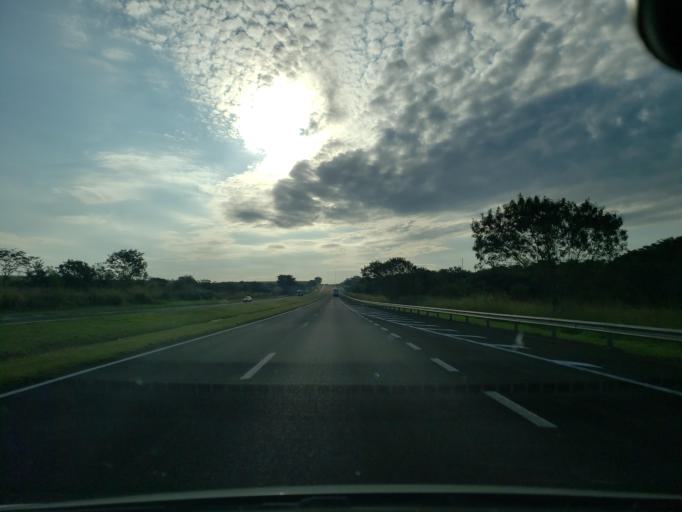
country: BR
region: Sao Paulo
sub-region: Valparaiso
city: Valparaiso
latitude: -21.1661
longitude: -50.9391
